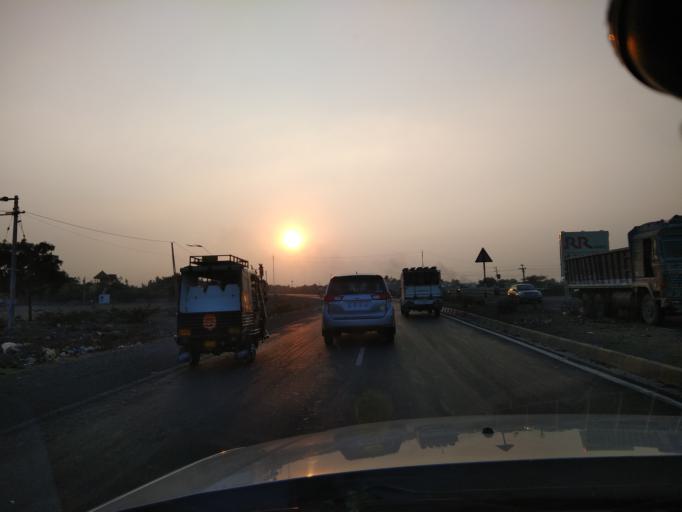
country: IN
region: Gujarat
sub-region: Jamnagar
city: Jamnagar
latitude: 22.4500
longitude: 70.0114
